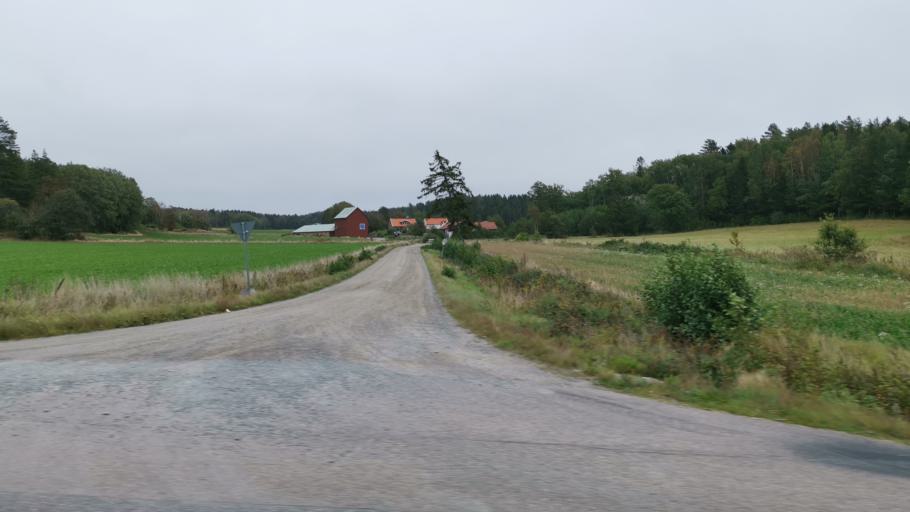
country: SE
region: Vaestra Goetaland
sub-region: Sotenas Kommun
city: Hunnebostrand
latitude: 58.5764
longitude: 11.3541
